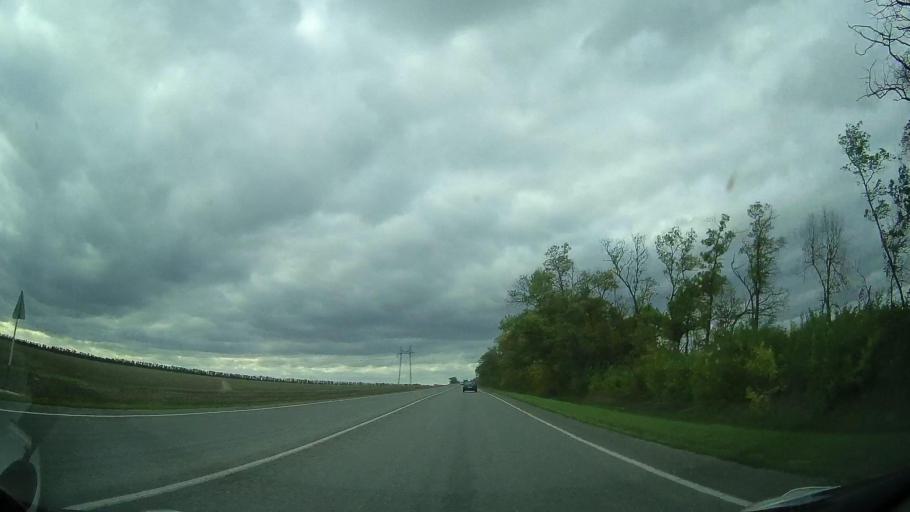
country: RU
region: Rostov
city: Zernograd
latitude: 46.8223
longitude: 40.2547
